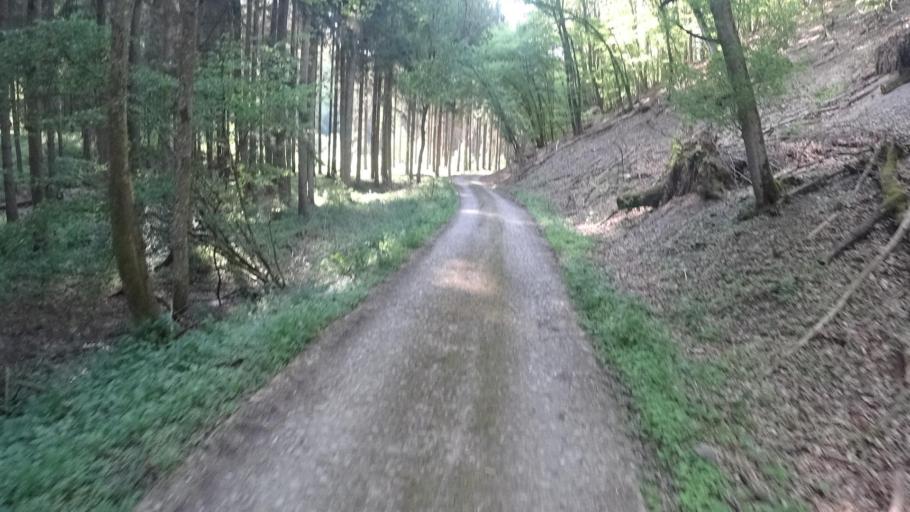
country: DE
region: Rheinland-Pfalz
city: Kirchsahr
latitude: 50.5012
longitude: 6.8951
